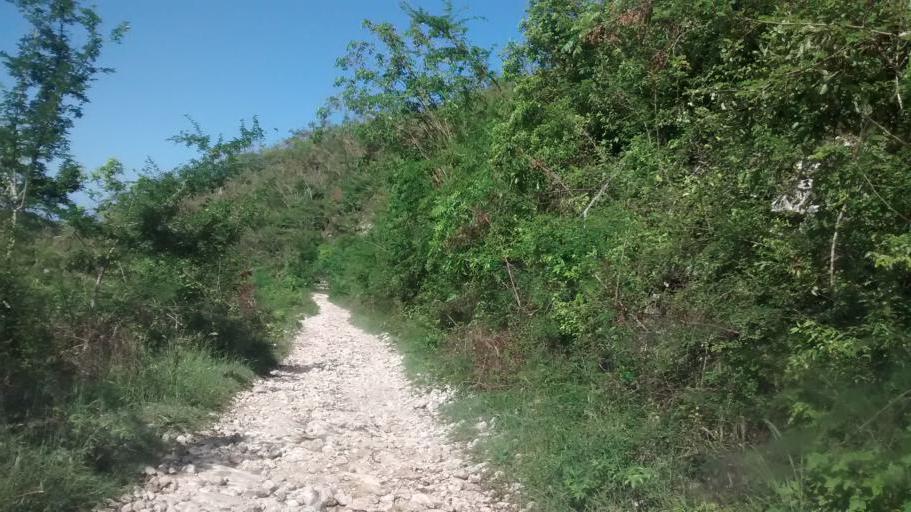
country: HT
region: Grandans
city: Corail
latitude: 18.5540
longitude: -73.9137
